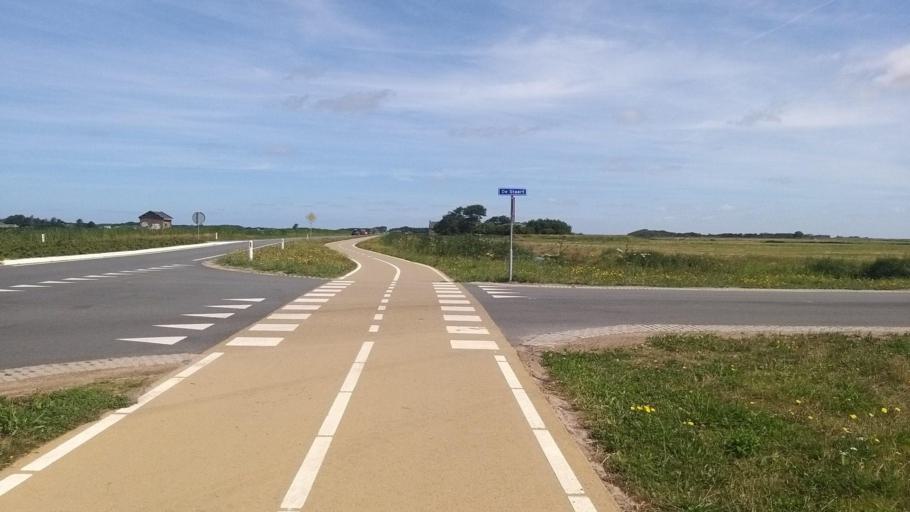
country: NL
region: North Holland
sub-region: Gemeente Texel
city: Den Burg
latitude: 53.0848
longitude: 4.7916
